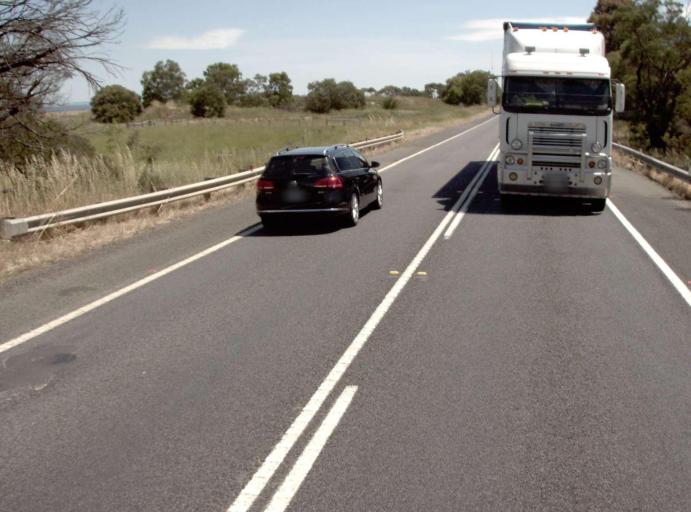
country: AU
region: Victoria
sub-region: Wellington
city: Heyfield
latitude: -38.1133
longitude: 146.8790
